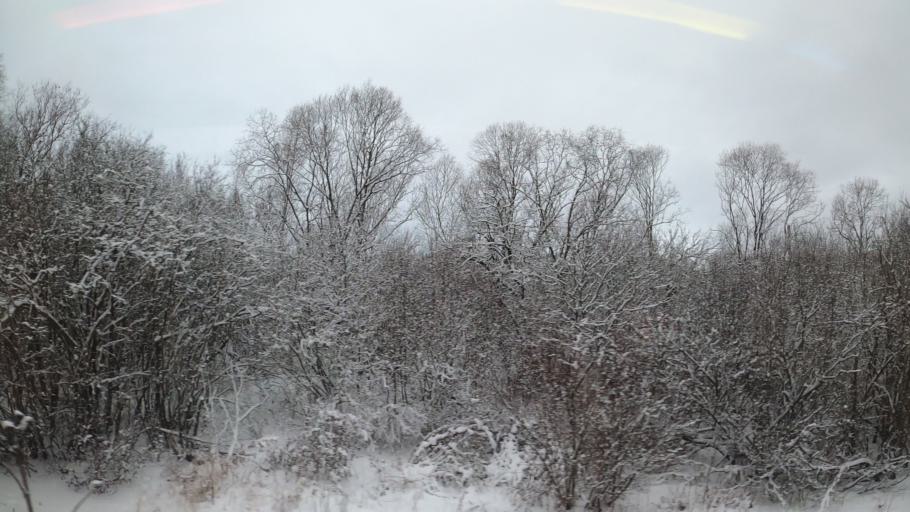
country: RU
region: Jaroslavl
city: Pereslavl'-Zalesskiy
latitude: 56.7304
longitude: 38.9014
